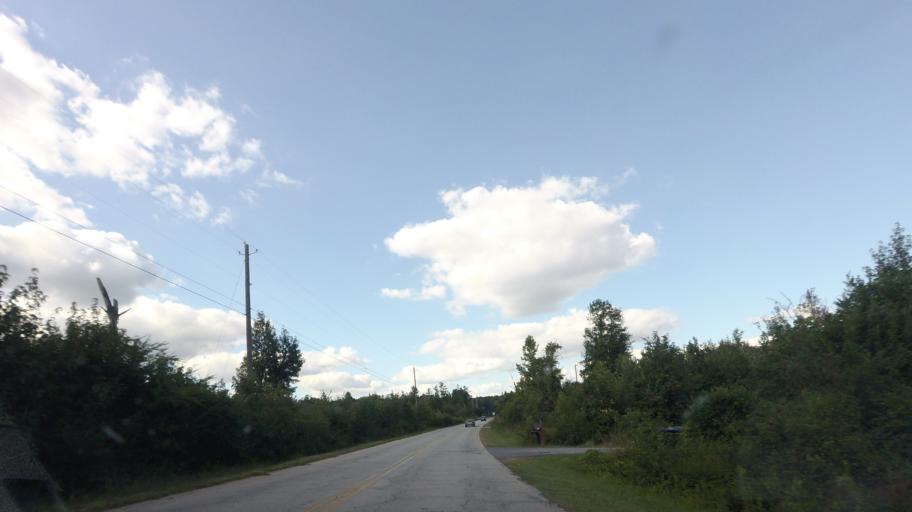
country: US
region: Georgia
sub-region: Lamar County
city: Barnesville
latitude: 33.0824
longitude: -84.1546
